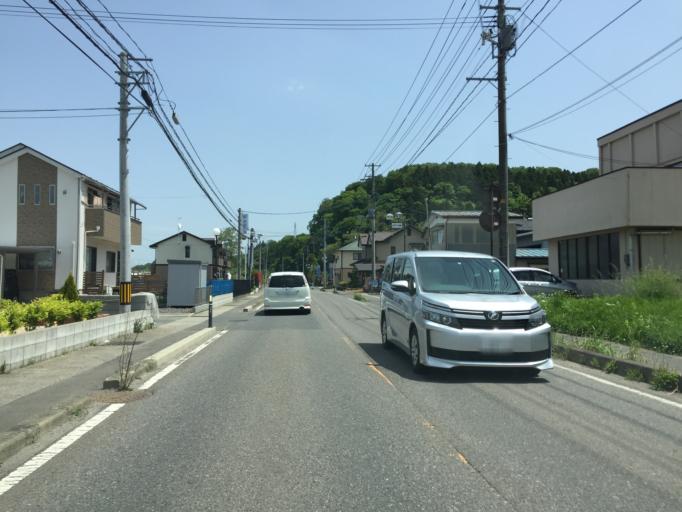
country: JP
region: Fukushima
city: Ishikawa
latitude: 37.1177
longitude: 140.2356
